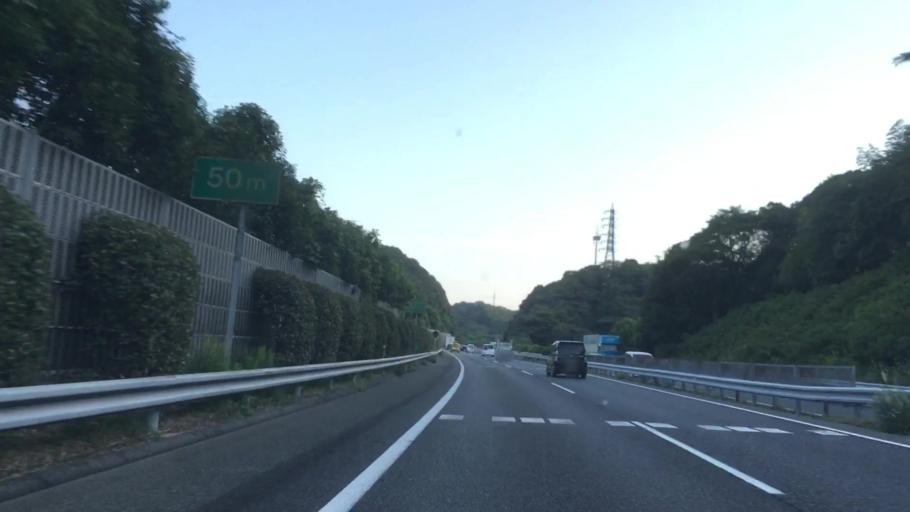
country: JP
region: Yamaguchi
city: Shimonoseki
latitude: 33.9005
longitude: 130.9715
